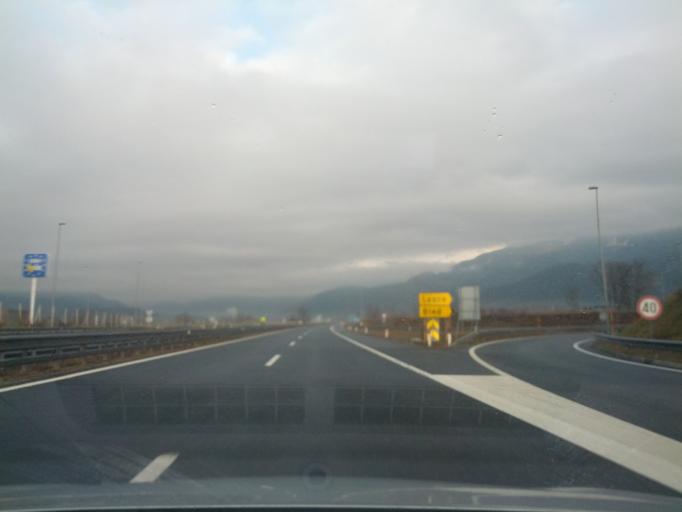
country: SI
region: Radovljica
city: Lesce
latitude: 46.3665
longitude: 14.1620
